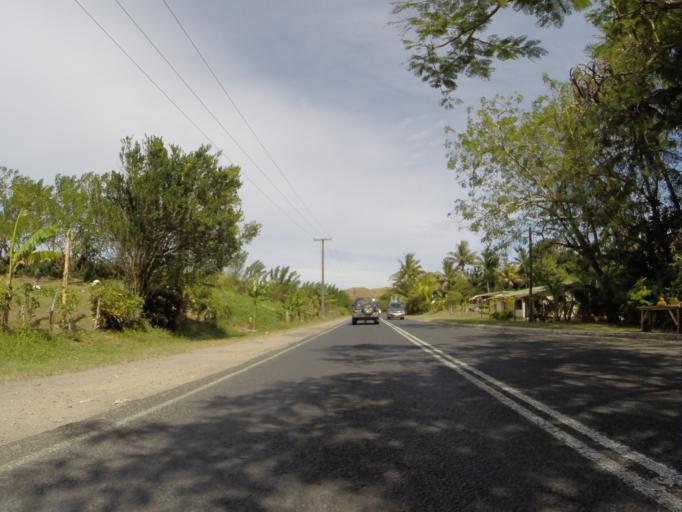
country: FJ
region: Western
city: Nadi
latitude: -18.1591
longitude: 177.4890
